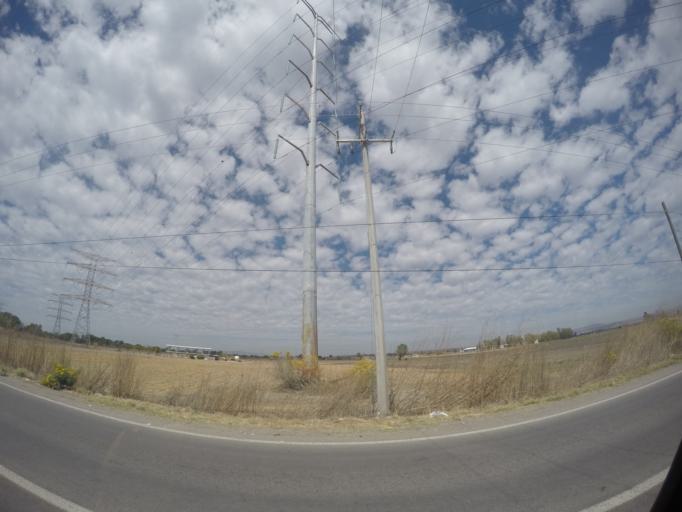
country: MX
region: Guanajuato
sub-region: Leon
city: El CERESO
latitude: 21.0287
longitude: -101.6959
